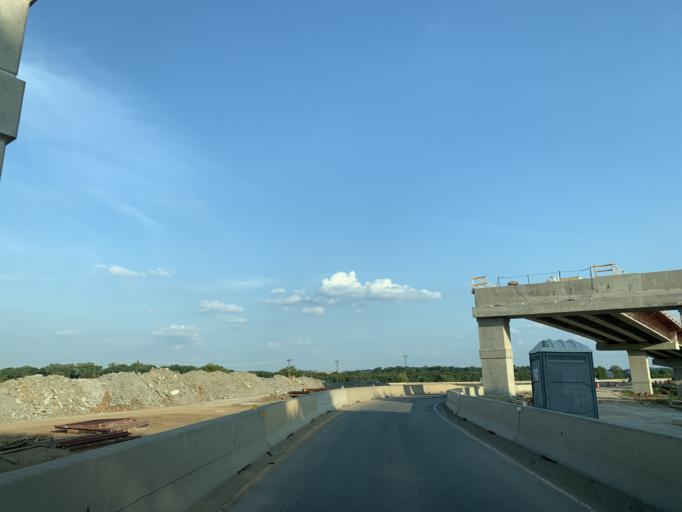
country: US
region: Texas
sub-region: Tarrant County
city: Richland Hills
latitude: 32.7965
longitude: -97.2130
